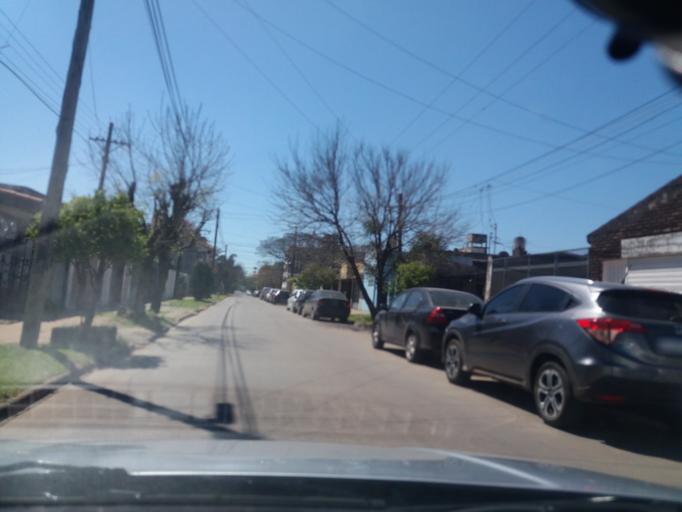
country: AR
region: Corrientes
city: Corrientes
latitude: -27.4864
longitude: -58.8446
